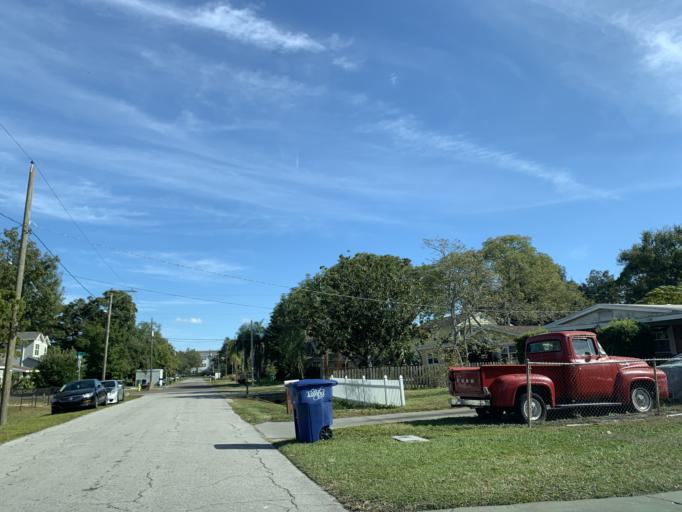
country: US
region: Florida
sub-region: Hillsborough County
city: Tampa
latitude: 27.8882
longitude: -82.4966
